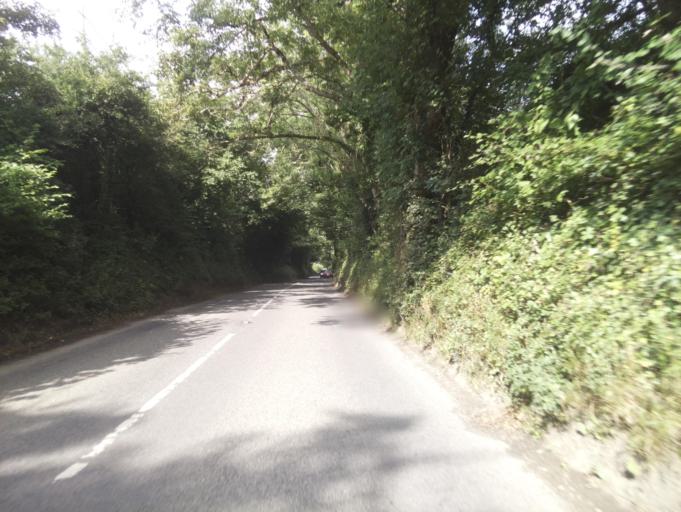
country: GB
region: England
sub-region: Somerset
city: Redlynch
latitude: 51.1064
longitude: -2.4372
